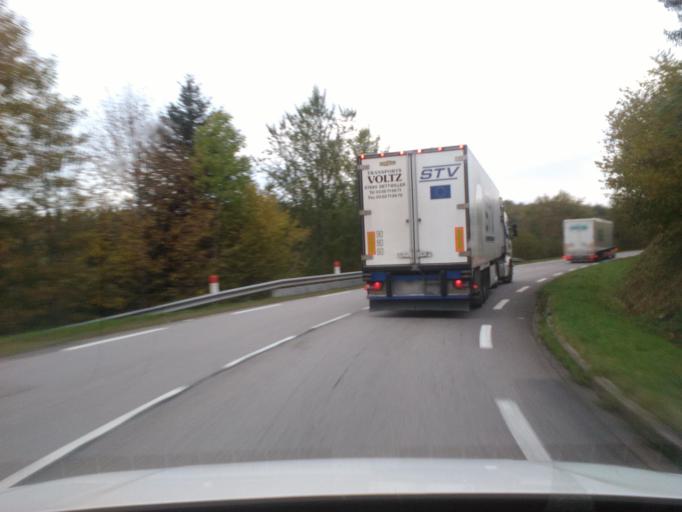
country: FR
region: Lorraine
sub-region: Departement des Vosges
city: Ban-de-Laveline
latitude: 48.3356
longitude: 7.0985
